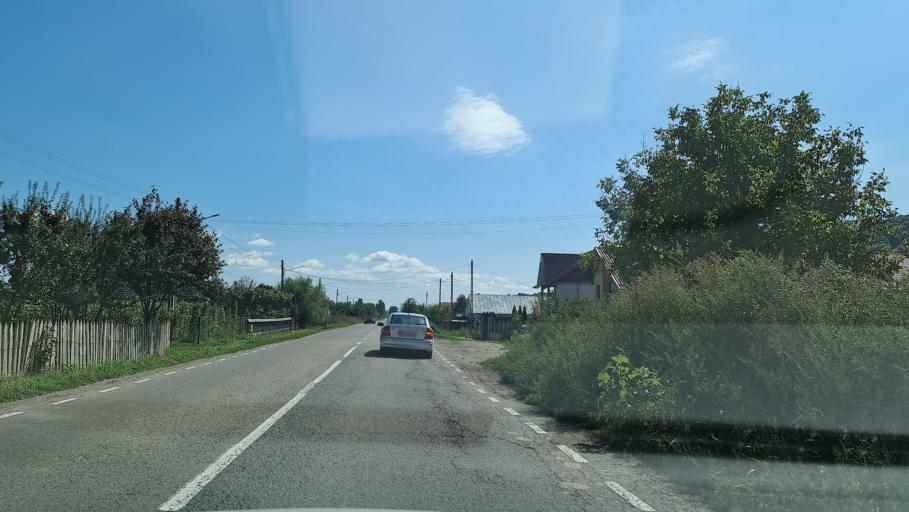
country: RO
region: Neamt
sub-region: Comuna Tazlau
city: Tazlau
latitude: 46.7089
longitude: 26.4868
